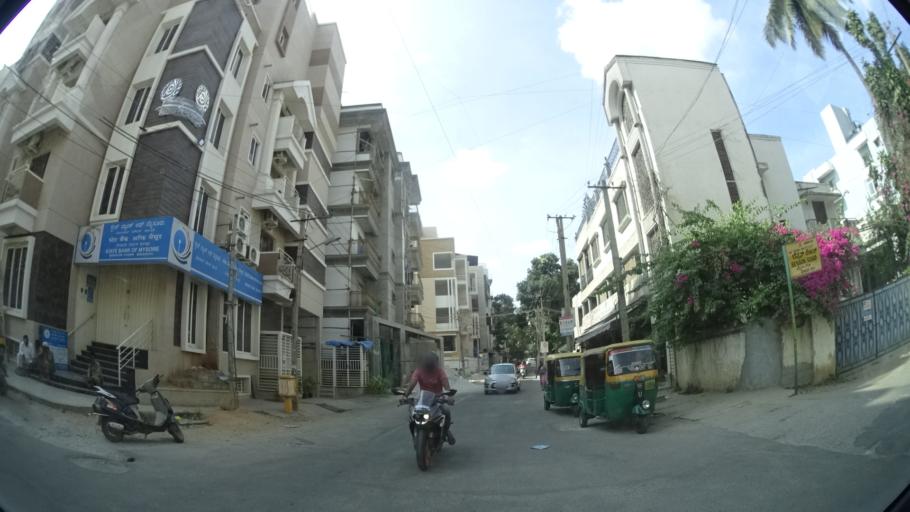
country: IN
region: Karnataka
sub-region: Bangalore Urban
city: Bangalore
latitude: 12.9968
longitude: 77.6043
